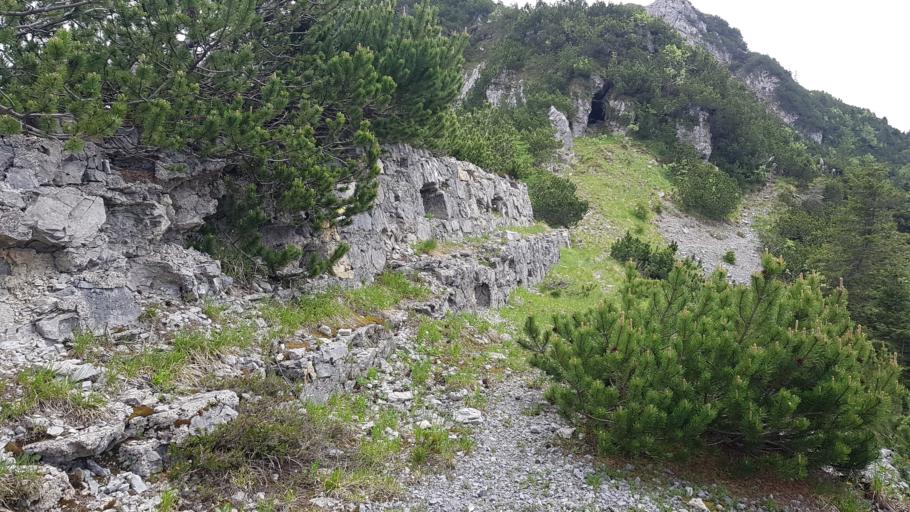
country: IT
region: Friuli Venezia Giulia
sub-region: Provincia di Udine
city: Paularo
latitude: 46.5203
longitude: 13.1796
